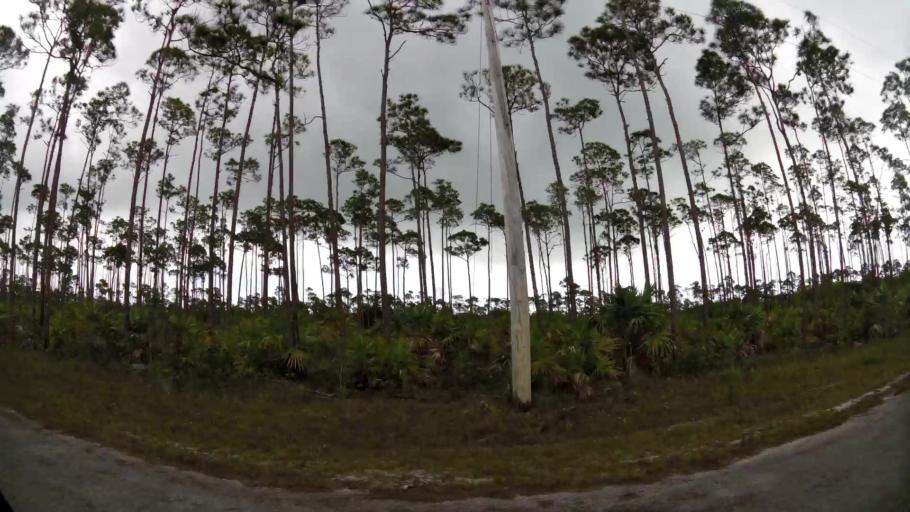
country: BS
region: Freeport
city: Lucaya
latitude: 26.5602
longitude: -78.5770
